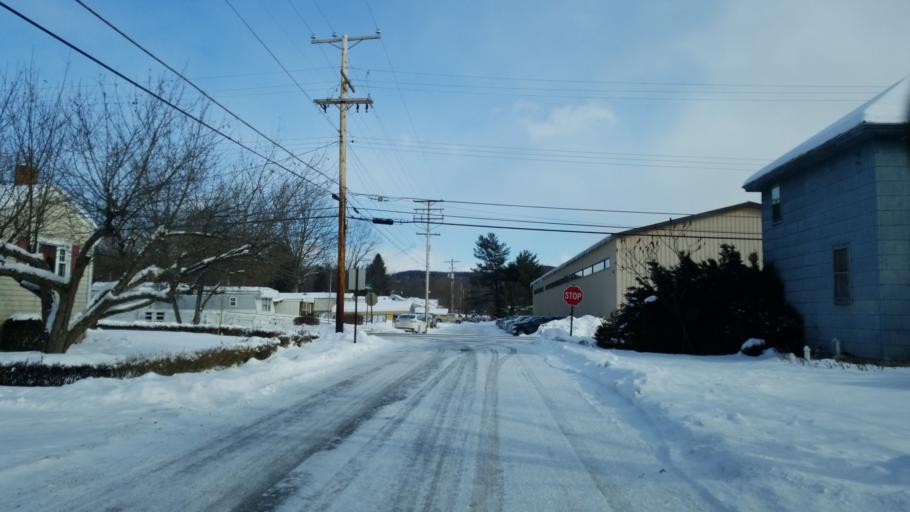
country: US
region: Pennsylvania
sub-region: Clearfield County
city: Hyde
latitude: 41.0027
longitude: -78.4641
